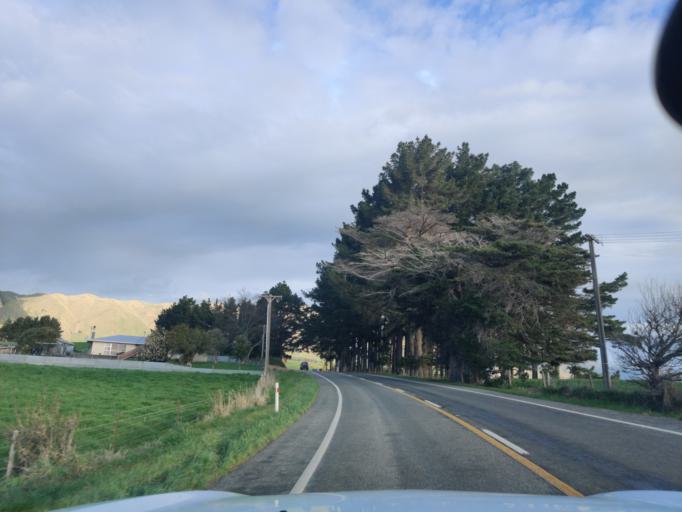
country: NZ
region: Manawatu-Wanganui
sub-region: Palmerston North City
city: Palmerston North
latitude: -40.4926
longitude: 175.4923
